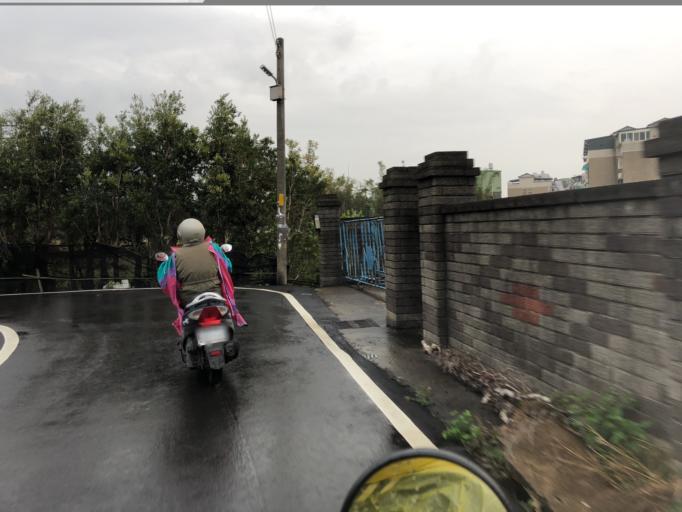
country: TW
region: Taiwan
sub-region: Hsinchu
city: Zhubei
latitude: 24.8493
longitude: 120.9922
